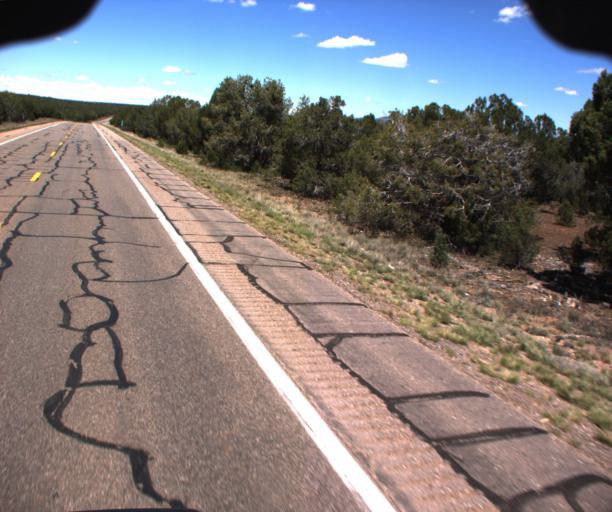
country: US
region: Arizona
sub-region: Yavapai County
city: Paulden
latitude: 35.0344
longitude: -112.3950
